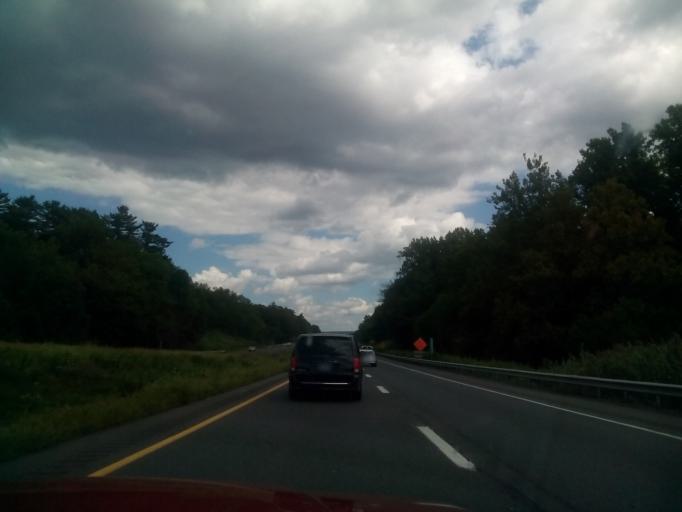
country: US
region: Pennsylvania
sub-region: Monroe County
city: Arlington Heights
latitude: 40.9945
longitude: -75.2598
